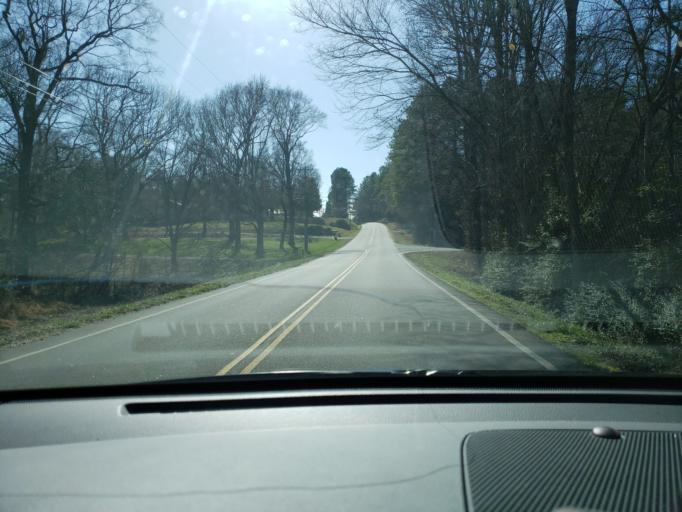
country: US
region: North Carolina
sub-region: Orange County
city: Chapel Hill
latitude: 35.9649
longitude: -79.0105
